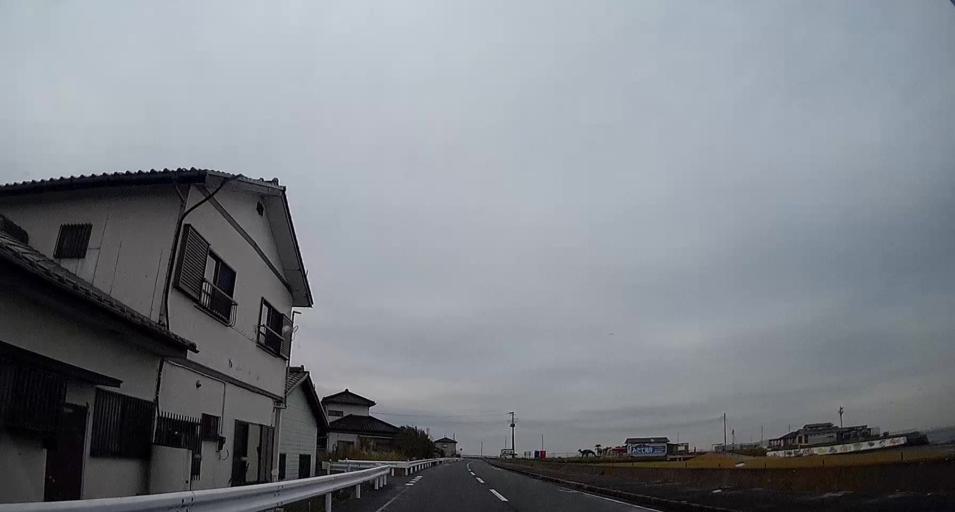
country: JP
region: Chiba
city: Kisarazu
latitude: 35.4318
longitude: 139.9070
